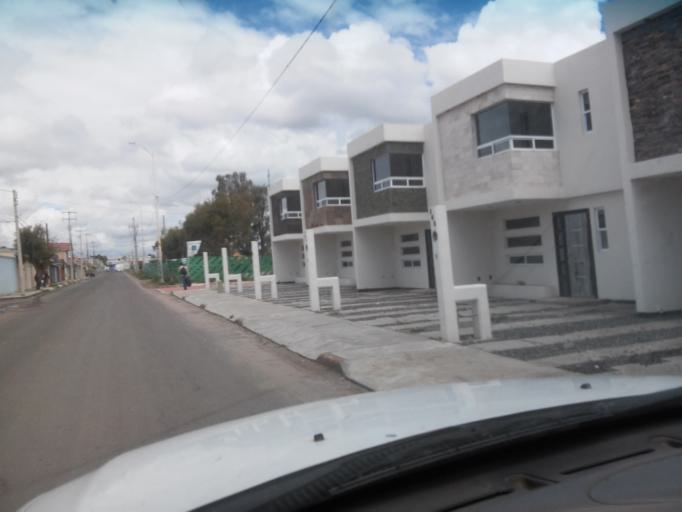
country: MX
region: Durango
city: Victoria de Durango
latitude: 24.0278
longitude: -104.6183
